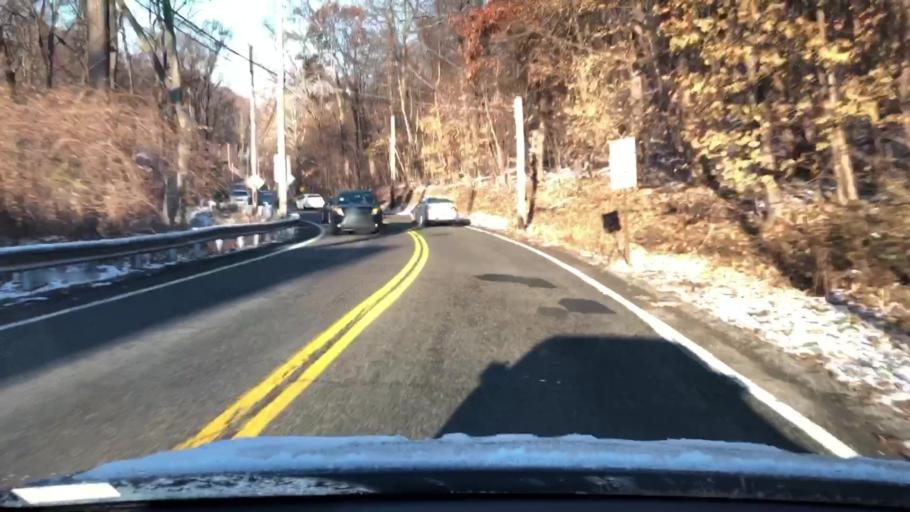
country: US
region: Pennsylvania
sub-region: Allegheny County
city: Blawnox
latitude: 40.4759
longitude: -79.8649
